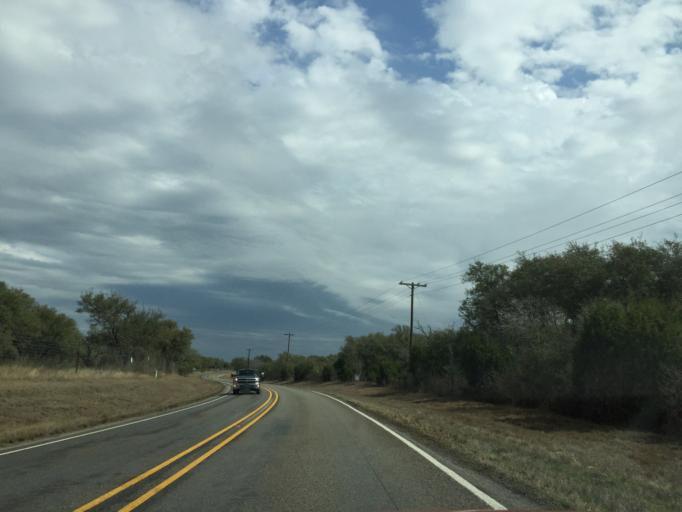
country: US
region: Texas
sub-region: Burnet County
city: Bertram
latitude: 30.6526
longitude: -97.9668
